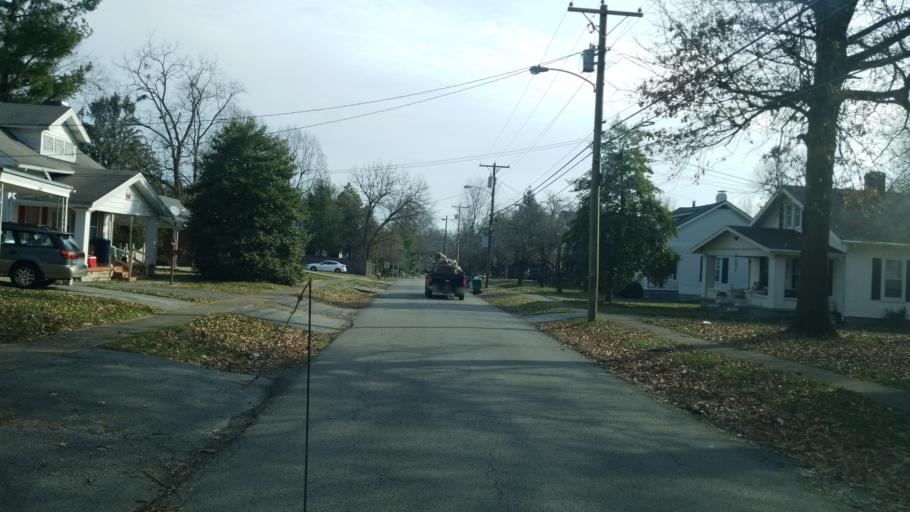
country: US
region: Kentucky
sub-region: Boyle County
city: Danville
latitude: 37.6498
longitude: -84.7847
